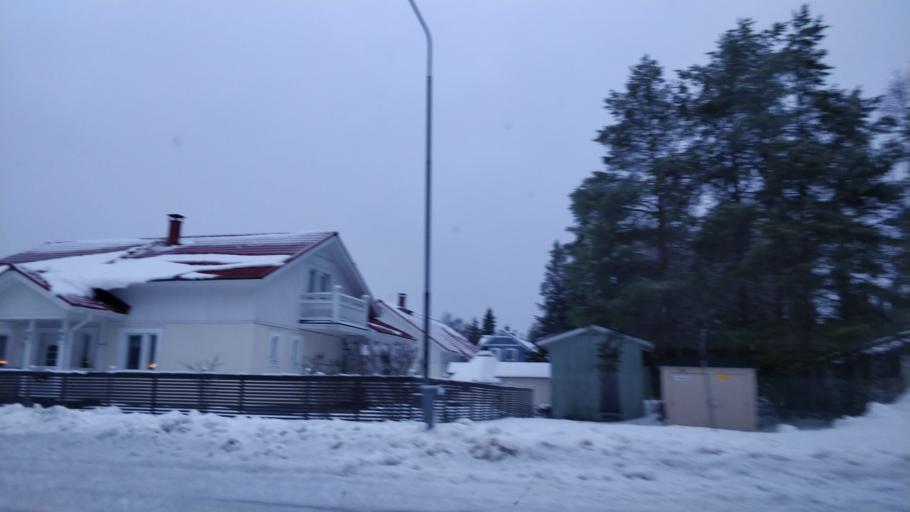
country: FI
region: Lapland
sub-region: Kemi-Tornio
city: Kemi
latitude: 65.7431
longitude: 24.6010
